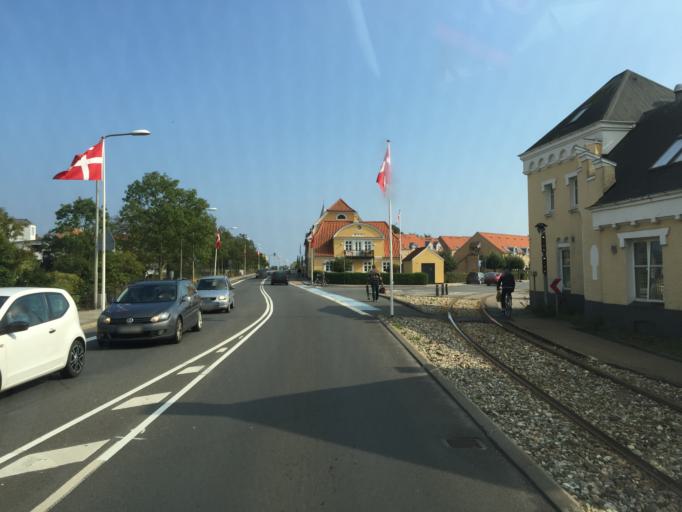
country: DK
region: South Denmark
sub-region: Nyborg Kommune
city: Nyborg
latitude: 55.3100
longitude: 10.7925
